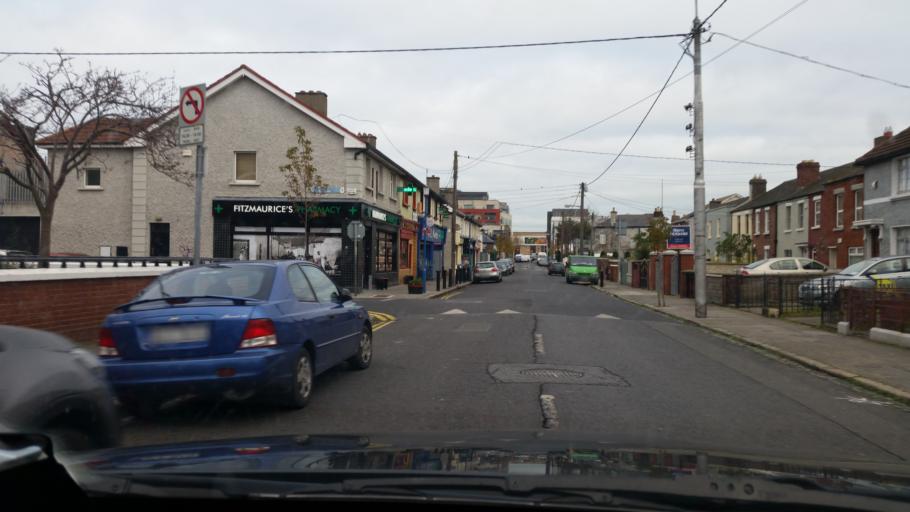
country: IE
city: Fairview
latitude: 53.3547
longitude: -6.2355
